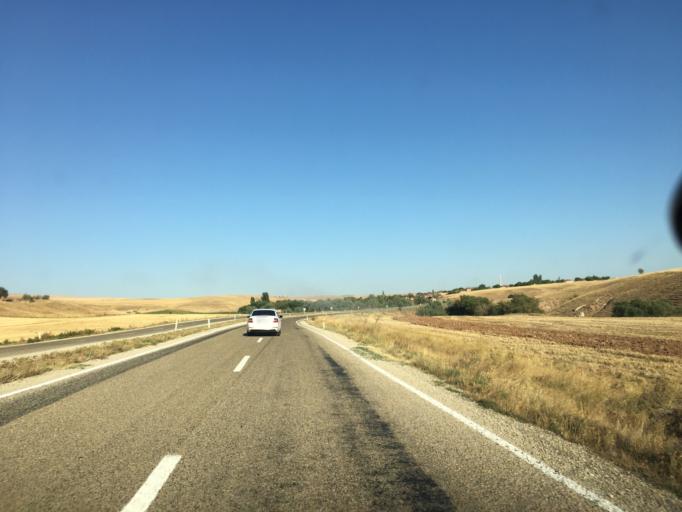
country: TR
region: Kirsehir
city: Mucur
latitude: 39.0150
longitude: 34.4565
